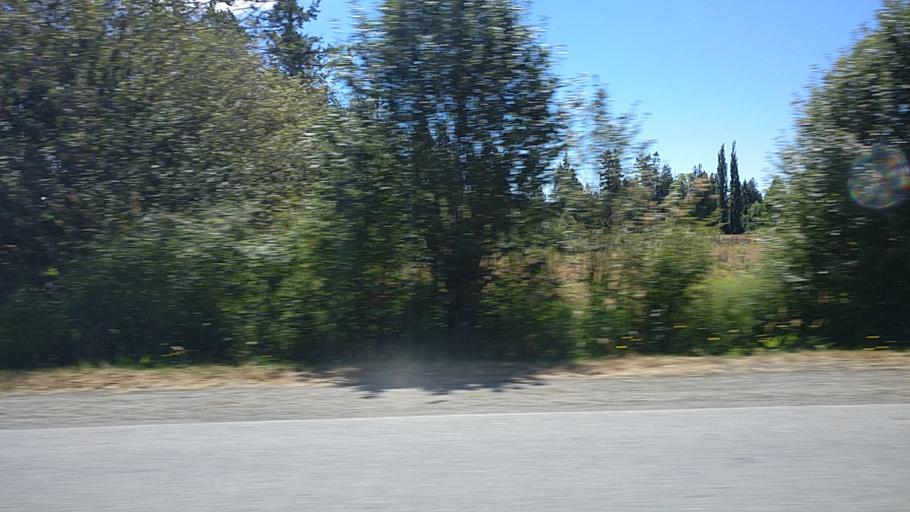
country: US
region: Washington
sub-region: Whatcom County
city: Blaine
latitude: 49.0167
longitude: -122.7326
